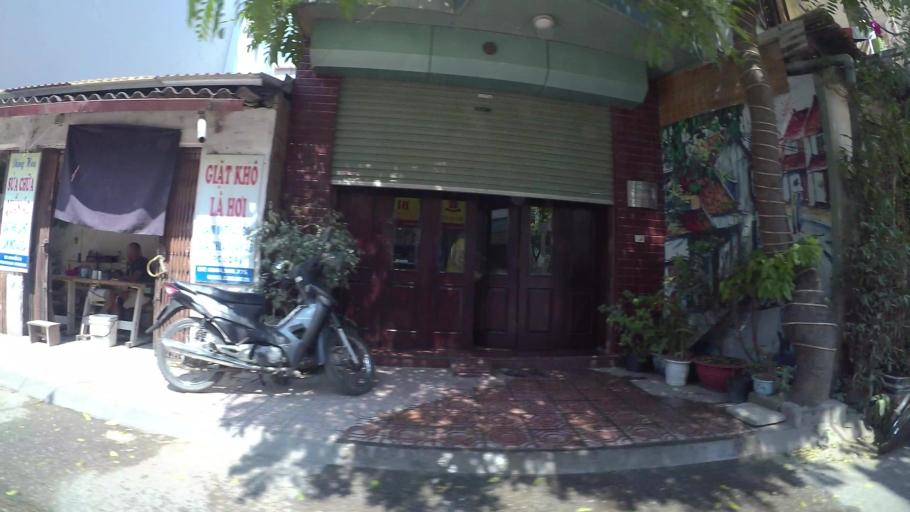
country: VN
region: Ha Noi
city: Hoan Kiem
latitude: 21.0528
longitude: 105.8780
